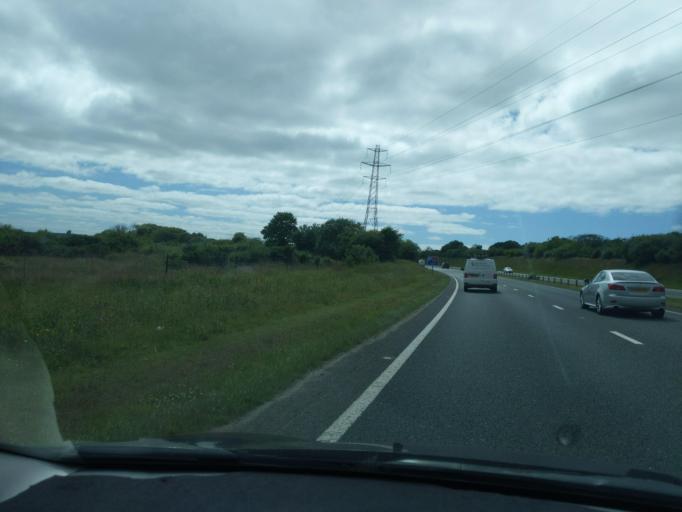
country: GB
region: England
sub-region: Cornwall
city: Saint Dennis
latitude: 50.4177
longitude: -4.8807
